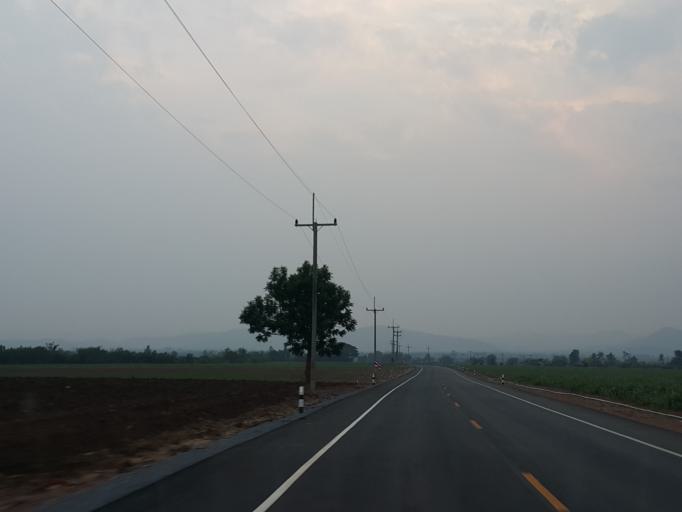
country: TH
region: Suphan Buri
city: Dan Chang
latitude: 14.9413
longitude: 99.6484
